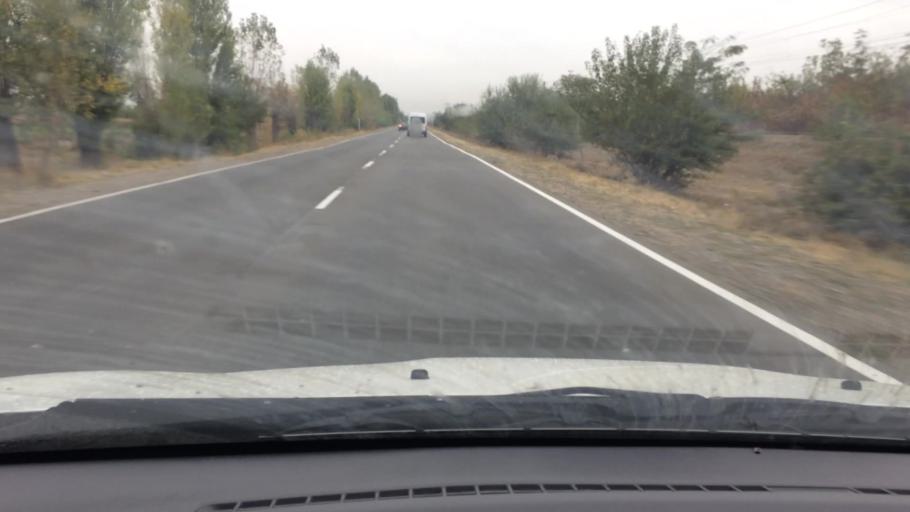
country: GE
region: Kvemo Kartli
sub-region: Marneuli
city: Marneuli
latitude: 41.4478
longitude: 44.8148
